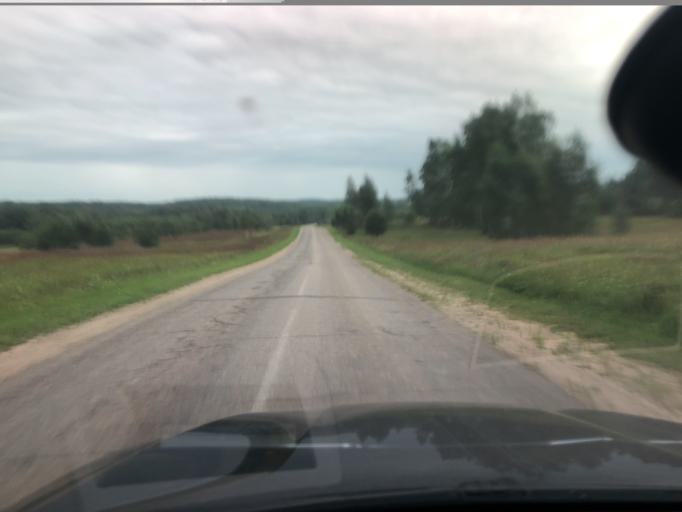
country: RU
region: Jaroslavl
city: Petrovsk
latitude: 56.9856
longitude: 39.1290
